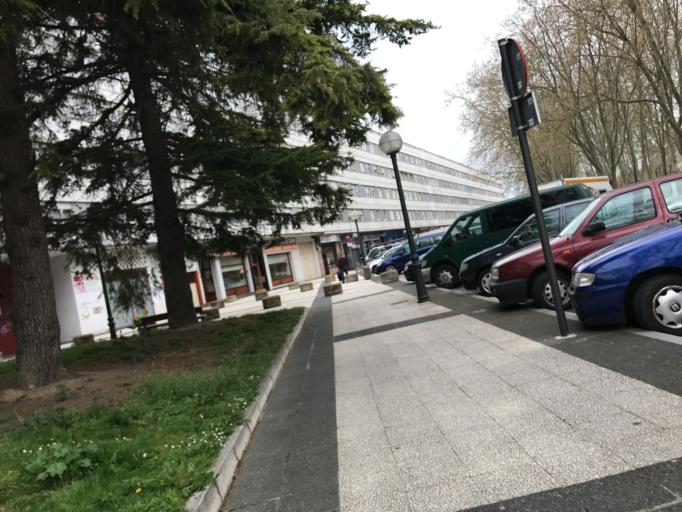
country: ES
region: Basque Country
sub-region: Provincia de Alava
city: Gasteiz / Vitoria
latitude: 42.8587
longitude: -2.6766
